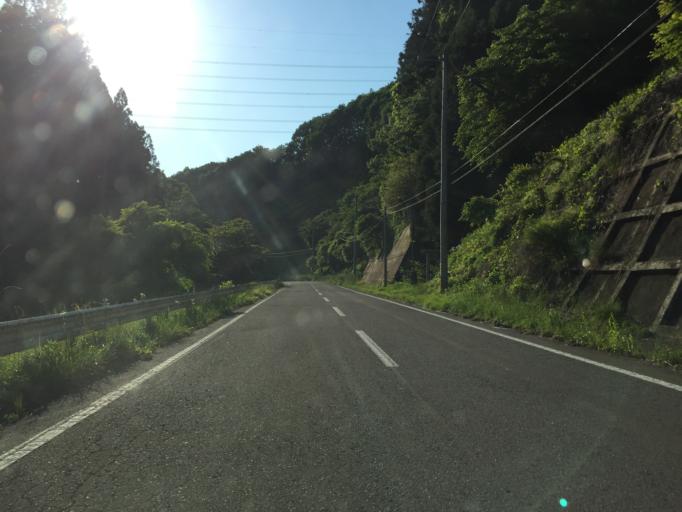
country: JP
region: Ibaraki
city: Daigo
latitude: 36.9220
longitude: 140.4932
